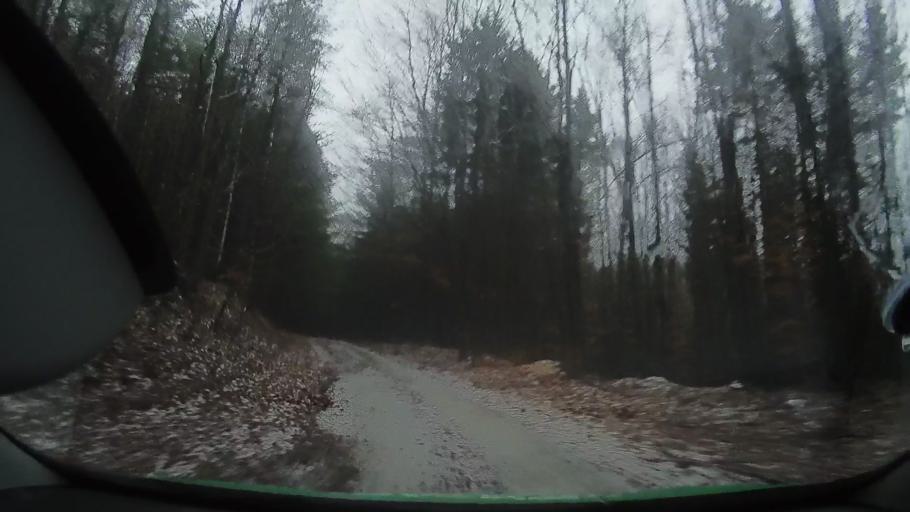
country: RO
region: Alba
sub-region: Comuna Avram Iancu
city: Avram Iancu
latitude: 46.3092
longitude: 22.7959
